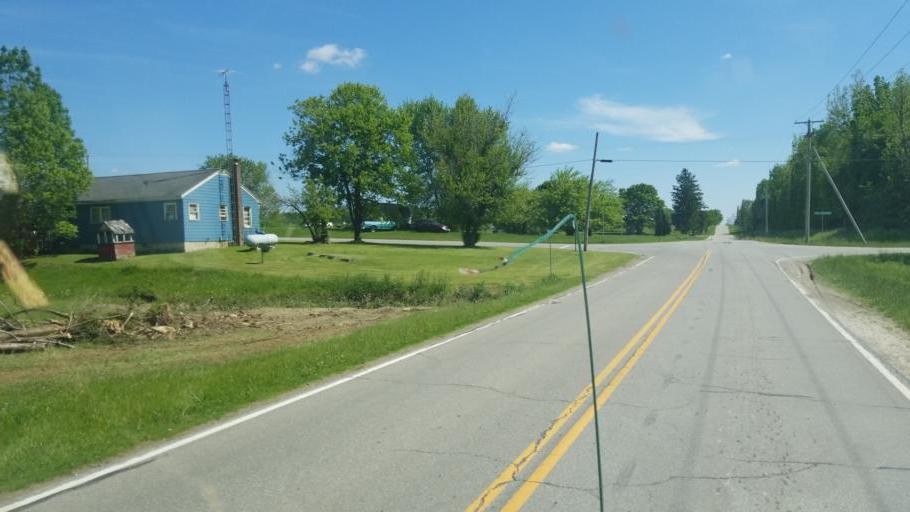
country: US
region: Ohio
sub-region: Crawford County
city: Bucyrus
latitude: 40.8636
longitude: -83.0550
